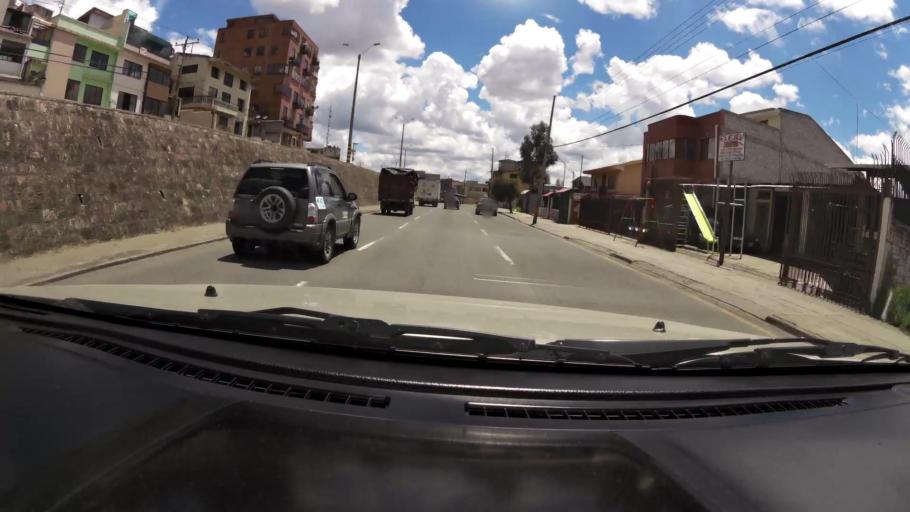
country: EC
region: Azuay
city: Cuenca
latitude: -2.8890
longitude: -79.0140
